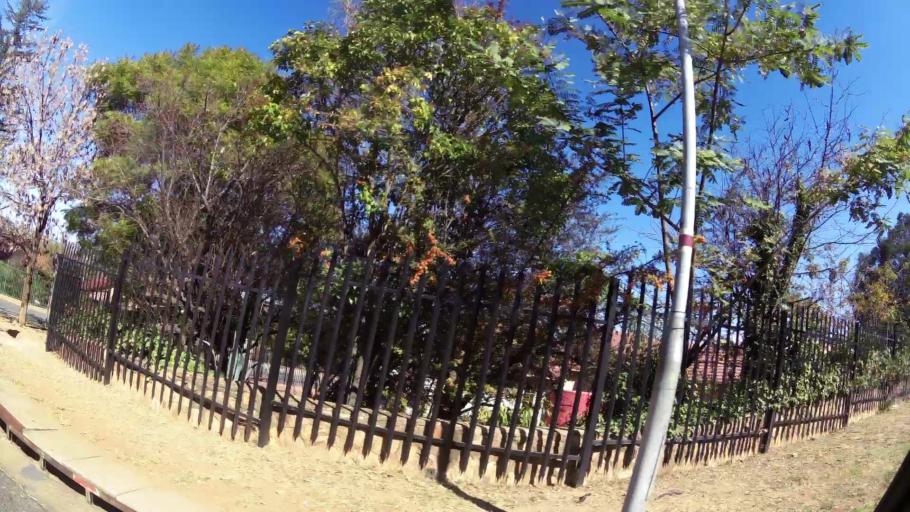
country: ZA
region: Gauteng
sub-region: City of Johannesburg Metropolitan Municipality
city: Johannesburg
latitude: -26.2631
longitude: 28.0043
